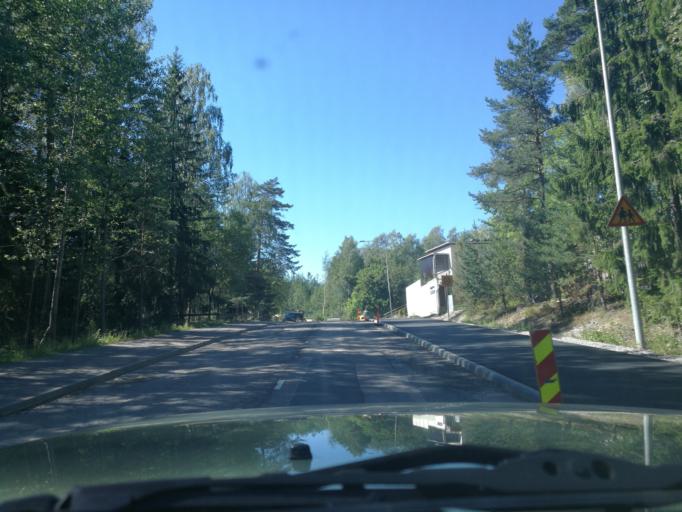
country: FI
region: Uusimaa
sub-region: Helsinki
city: Kerava
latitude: 60.3454
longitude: 25.1148
